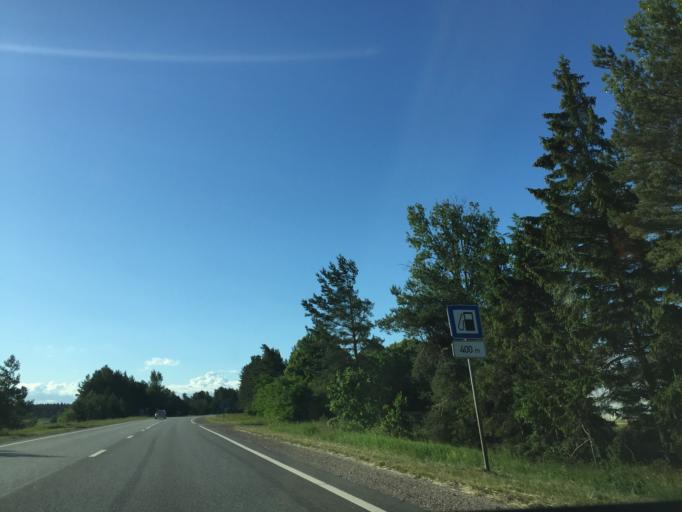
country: LV
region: Ventspils
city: Ventspils
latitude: 57.4001
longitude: 21.6892
